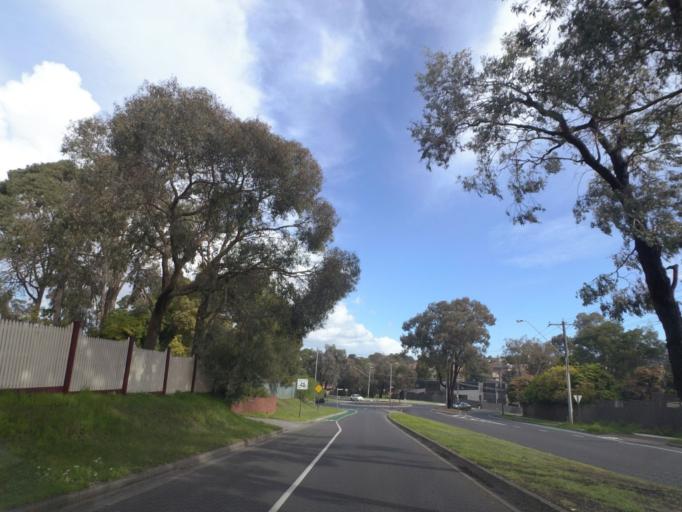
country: AU
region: Victoria
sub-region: Whitehorse
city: Vermont South
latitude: -37.8503
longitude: 145.1885
